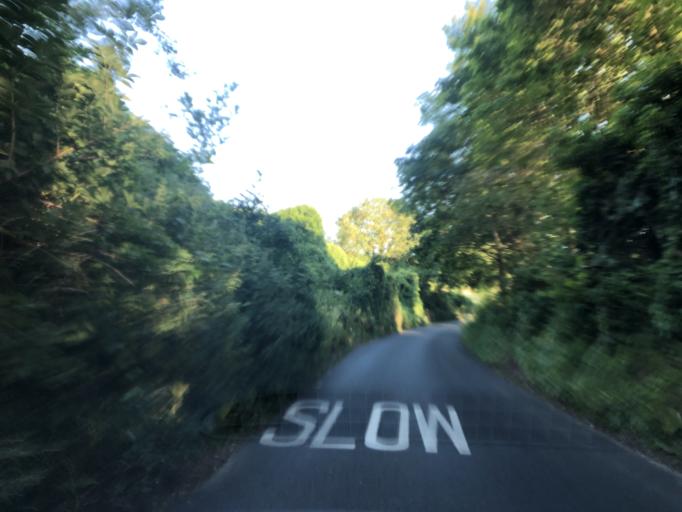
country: GB
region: England
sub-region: Isle of Wight
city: Shalfleet
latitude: 50.6556
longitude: -1.4003
